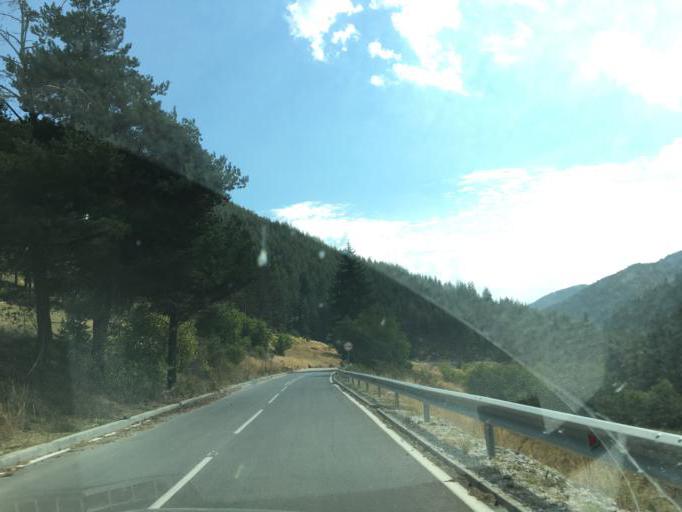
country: BG
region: Pazardzhik
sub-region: Obshtina Batak
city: Batak
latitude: 41.8909
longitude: 24.3298
